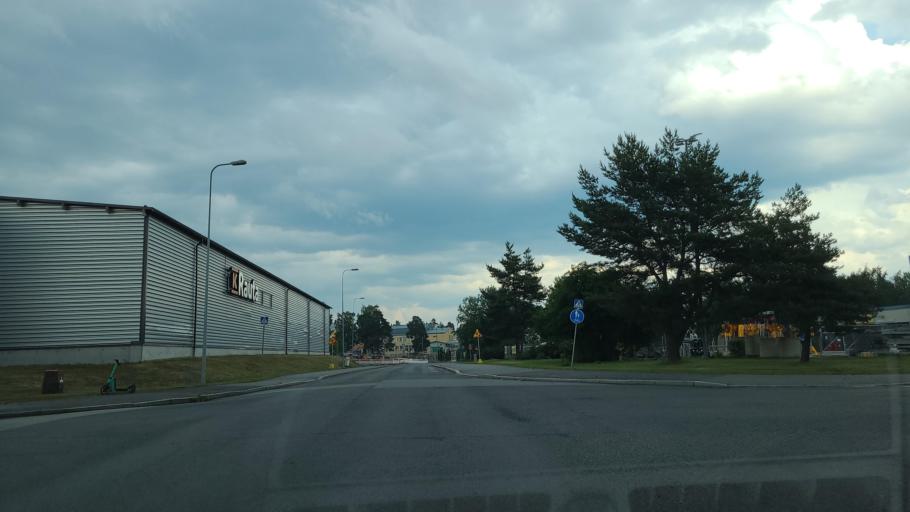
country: FI
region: Ostrobothnia
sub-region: Vaasa
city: Vaasa
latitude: 63.0964
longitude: 21.6369
